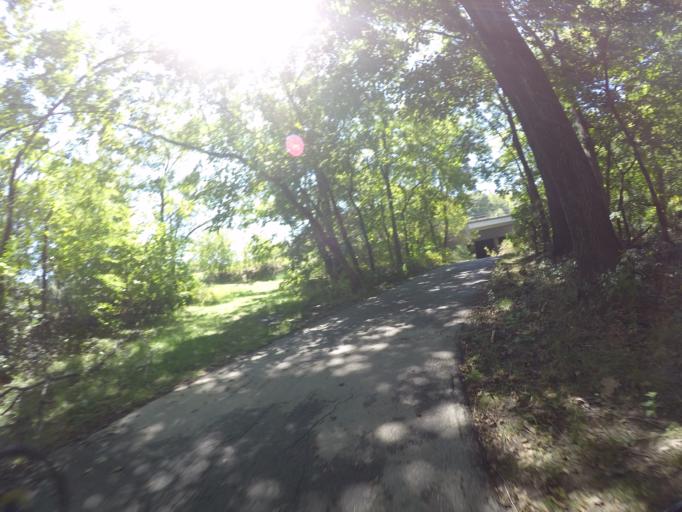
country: US
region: Kansas
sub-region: Johnson County
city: Lenexa
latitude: 38.9280
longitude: -94.6967
